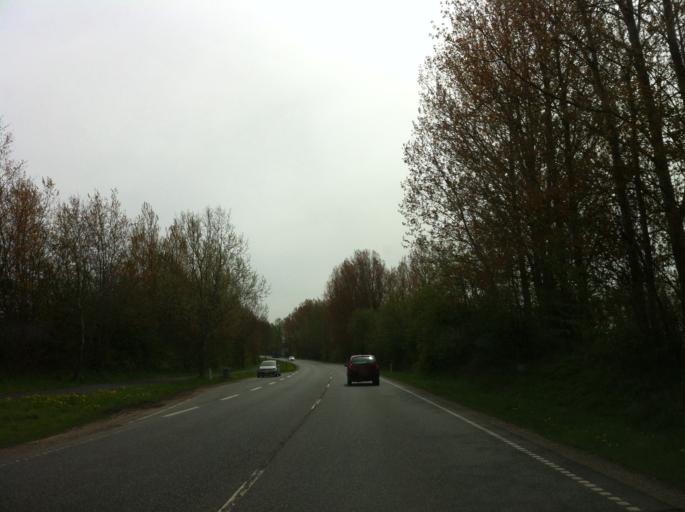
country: DK
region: Capital Region
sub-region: Frederikssund Kommune
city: Slangerup
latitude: 55.8393
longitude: 12.1603
